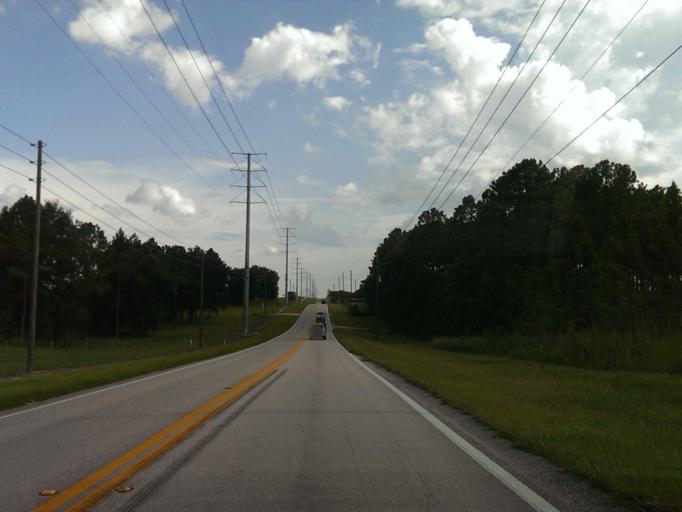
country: US
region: Florida
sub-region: Orange County
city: Oakland
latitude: 28.4560
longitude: -81.6364
